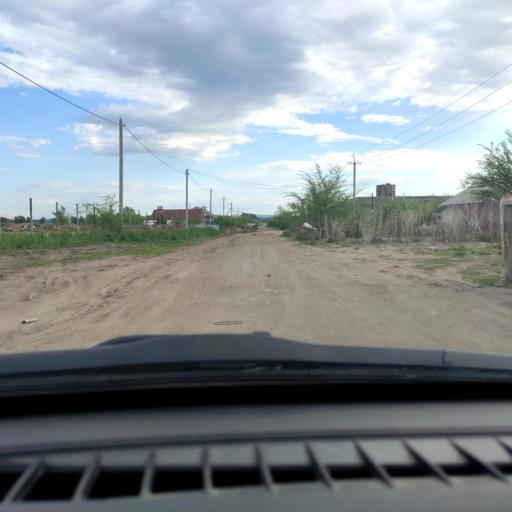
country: RU
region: Samara
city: Tol'yatti
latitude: 53.5763
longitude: 49.4144
